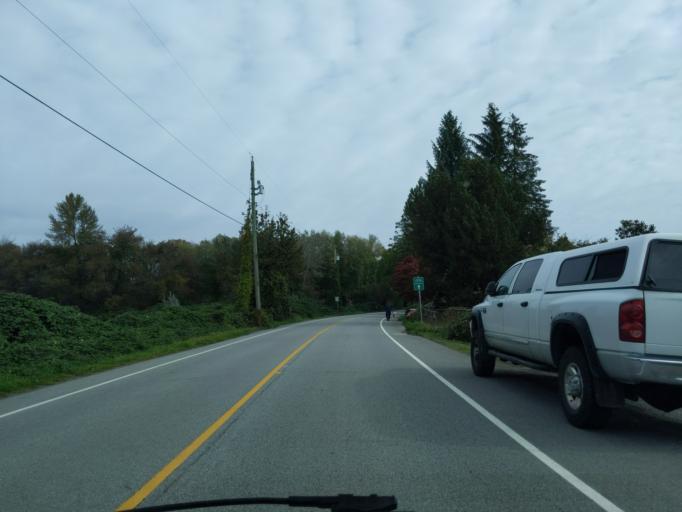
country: CA
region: British Columbia
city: Maple Ridge
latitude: 49.2056
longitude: -122.6210
